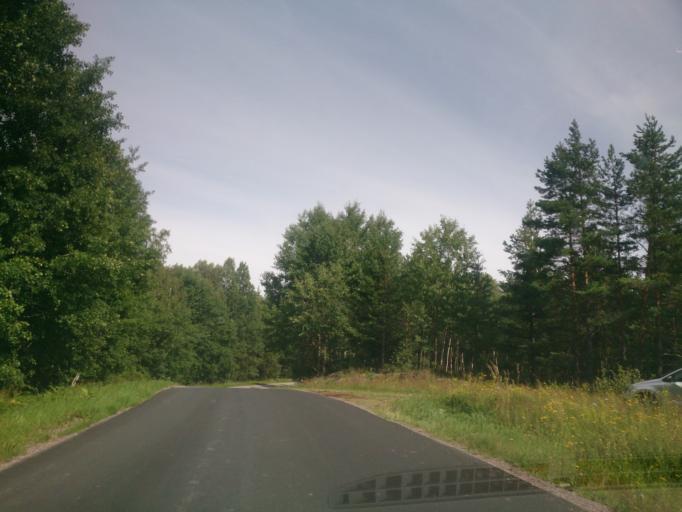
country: SE
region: OEstergoetland
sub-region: Valdemarsviks Kommun
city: Gusum
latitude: 58.3078
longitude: 16.5469
